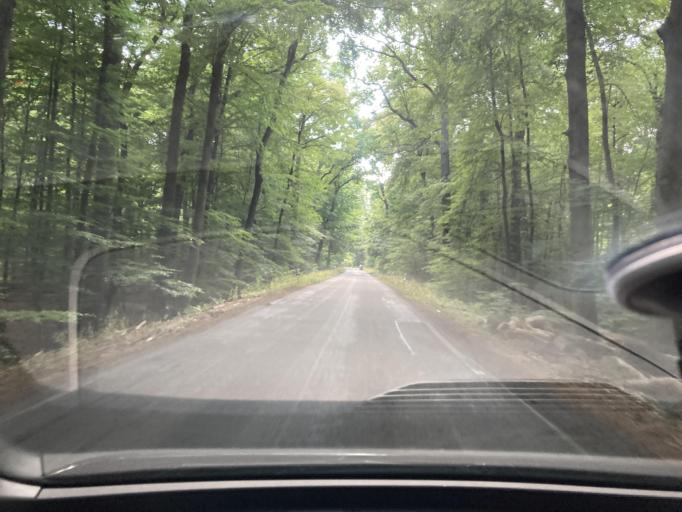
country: DE
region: Hesse
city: Obertshausen
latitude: 50.1012
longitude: 8.8810
